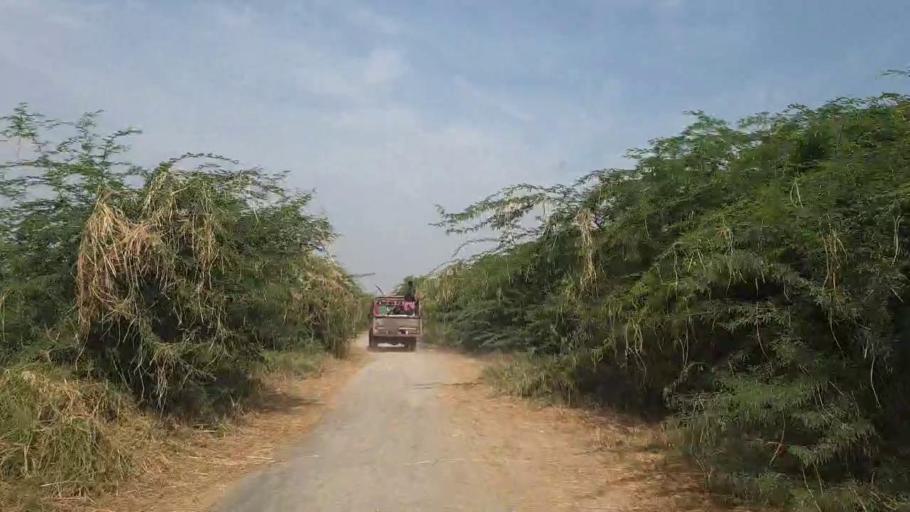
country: PK
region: Sindh
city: Tando Bago
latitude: 24.9148
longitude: 68.9955
